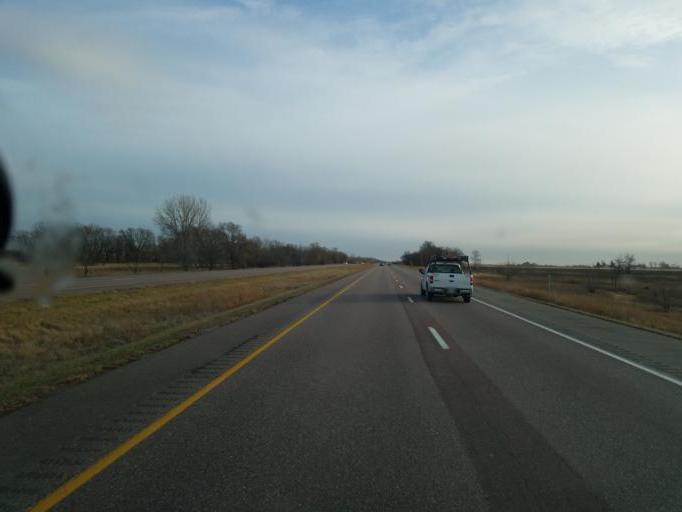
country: US
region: Nebraska
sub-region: Thurston County
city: Macy
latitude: 42.1520
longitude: -96.2204
